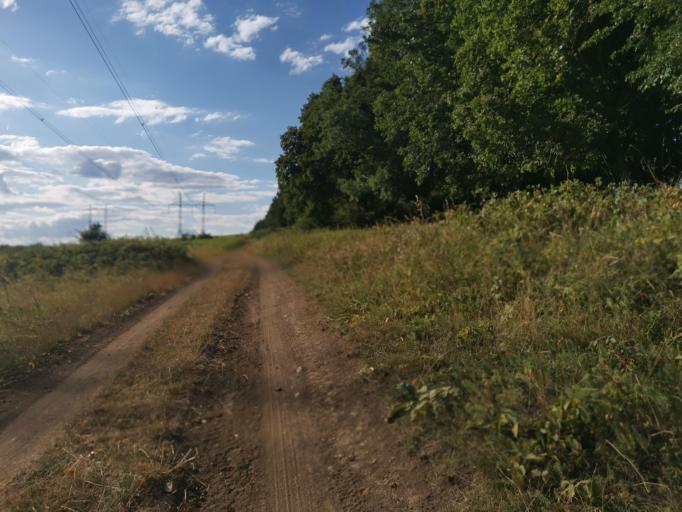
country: CZ
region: South Moravian
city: Sudomerice
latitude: 48.8096
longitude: 17.2906
